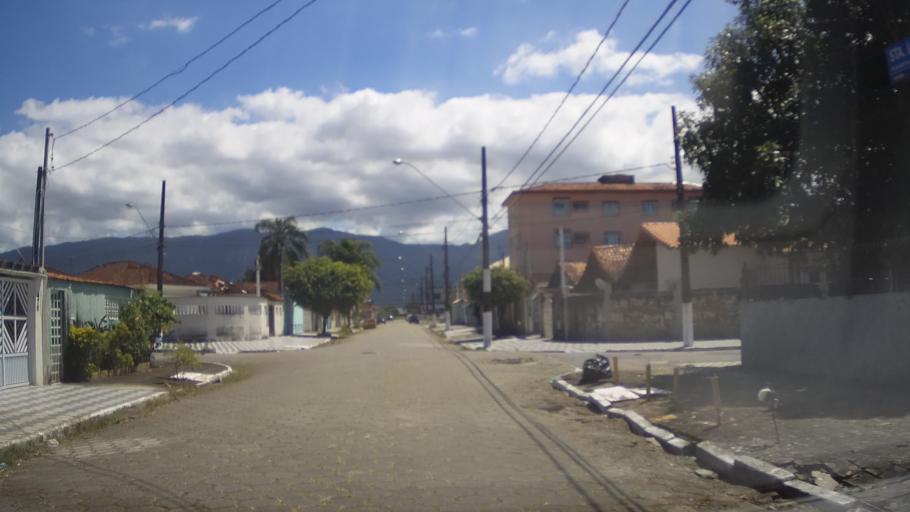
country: BR
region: Sao Paulo
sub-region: Mongagua
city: Mongagua
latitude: -24.0431
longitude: -46.5176
